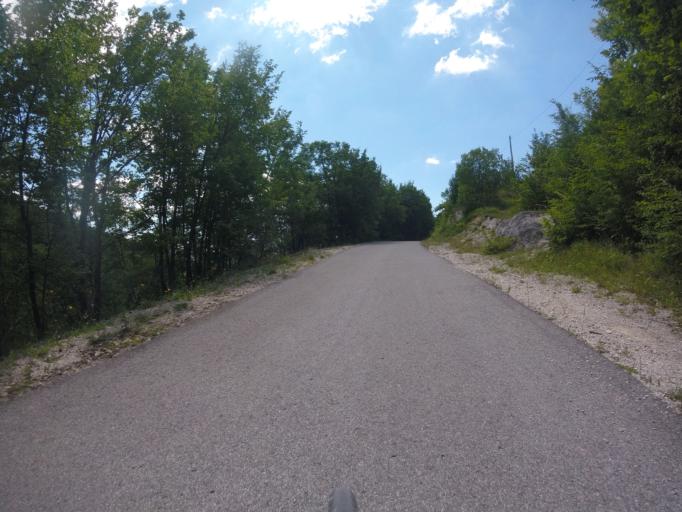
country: SI
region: Kostanjevica na Krki
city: Kostanjevica na Krki
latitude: 45.7607
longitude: 15.3969
